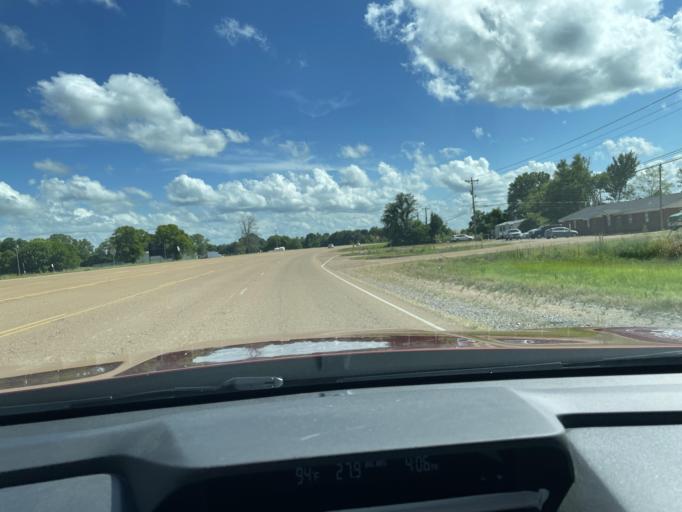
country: US
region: Mississippi
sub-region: Humphreys County
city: Belzoni
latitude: 33.1633
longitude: -90.4993
